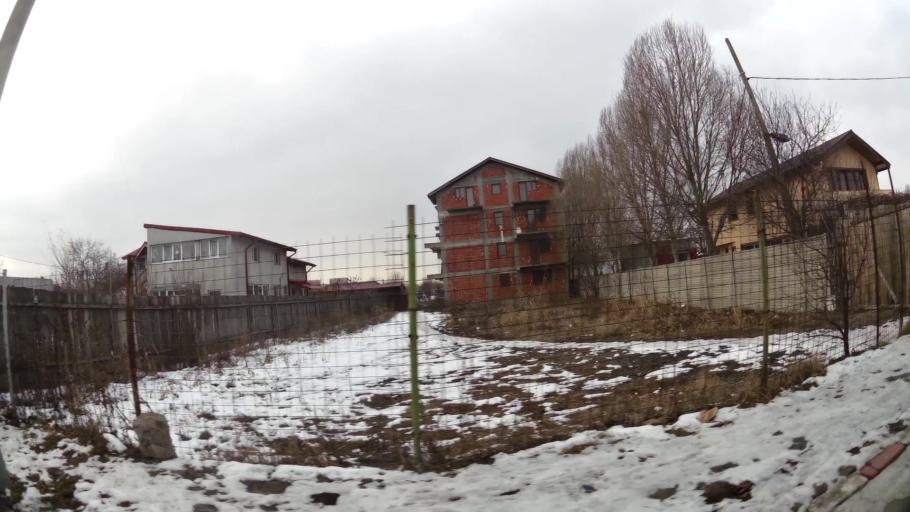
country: RO
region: Ilfov
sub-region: Voluntari City
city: Voluntari
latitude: 44.4905
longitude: 26.1640
